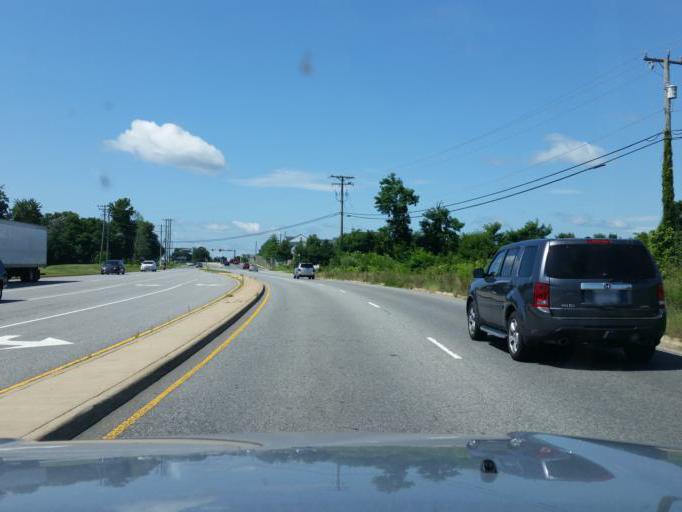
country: US
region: Virginia
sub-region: Stafford County
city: Falmouth
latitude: 38.3090
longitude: -77.5144
